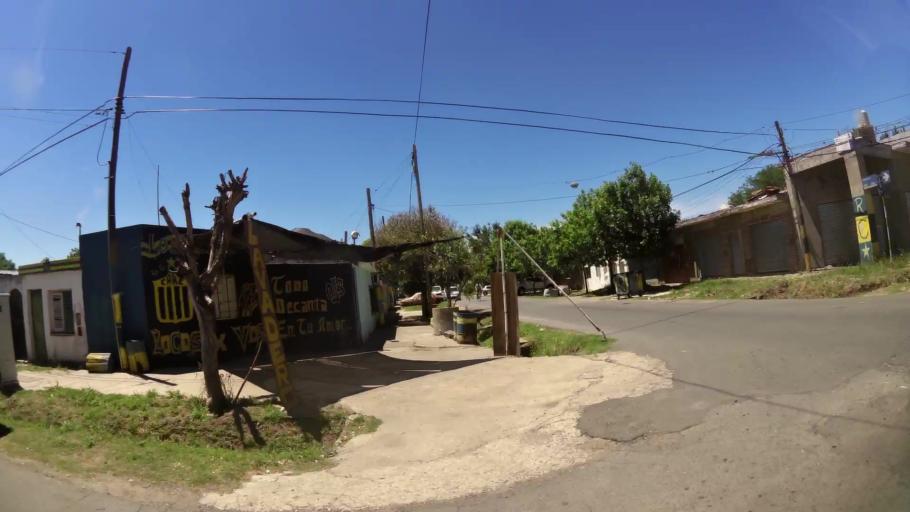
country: AR
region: Santa Fe
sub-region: Departamento de Rosario
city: Rosario
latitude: -32.9567
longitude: -60.7050
